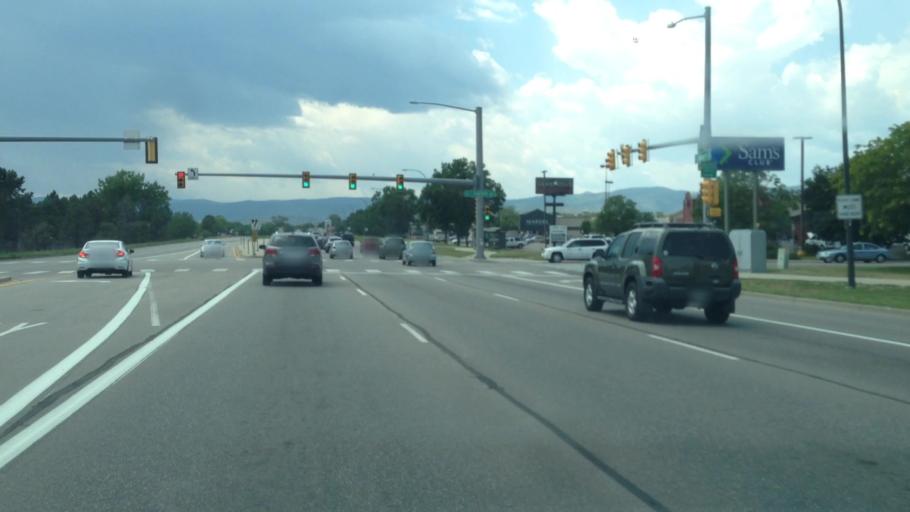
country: US
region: Colorado
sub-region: Jefferson County
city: Columbine
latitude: 39.6278
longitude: -105.0881
